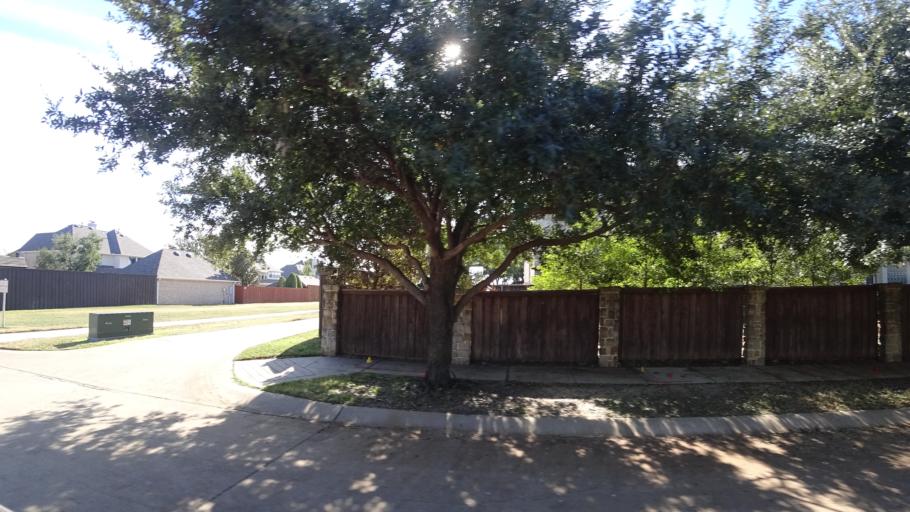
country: US
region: Texas
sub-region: Denton County
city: The Colony
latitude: 33.0361
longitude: -96.8927
